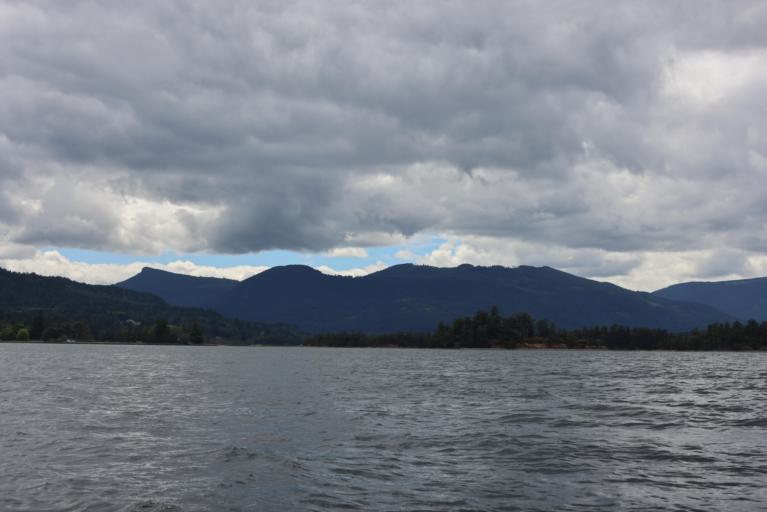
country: CA
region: British Columbia
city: North Cowichan
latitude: 48.8907
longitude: -123.6356
